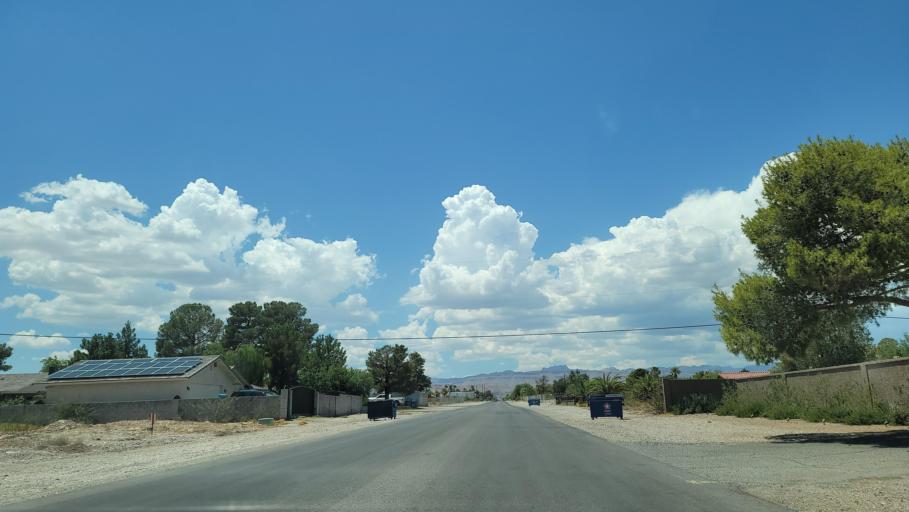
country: US
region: Nevada
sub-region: Clark County
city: Spring Valley
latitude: 36.0782
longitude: -115.2276
